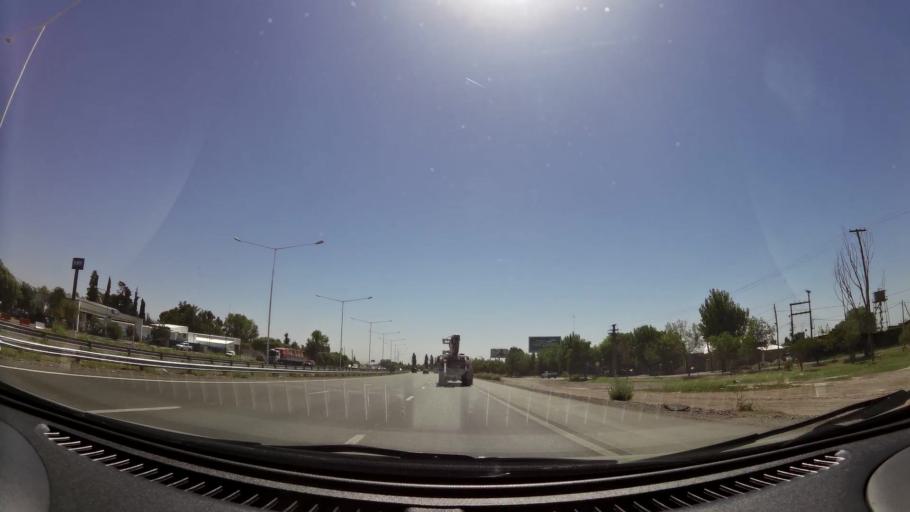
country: AR
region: Mendoza
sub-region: Departamento de Godoy Cruz
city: Godoy Cruz
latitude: -32.9504
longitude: -68.8344
